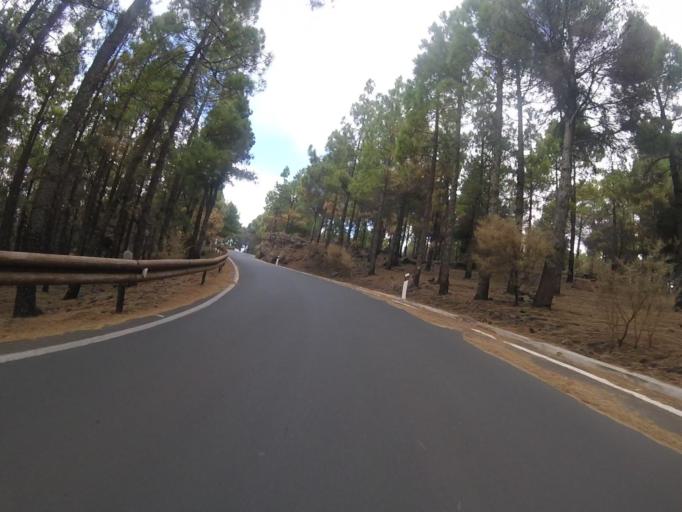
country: ES
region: Canary Islands
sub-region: Provincia de Las Palmas
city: Tejeda
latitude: 27.9731
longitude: -15.5740
